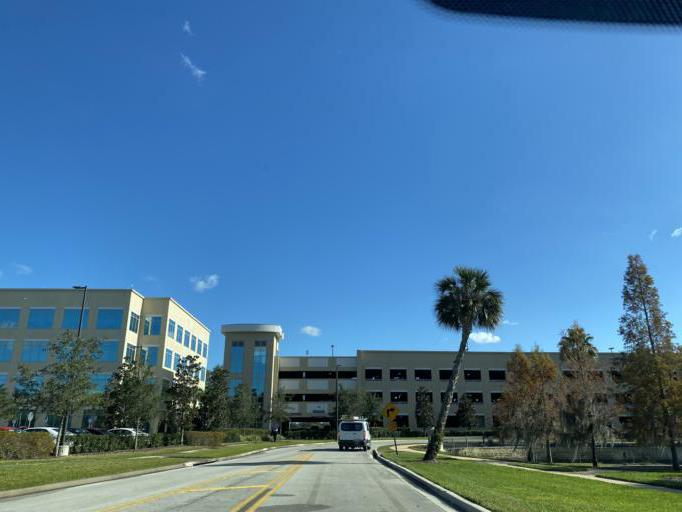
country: US
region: Florida
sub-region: Seminole County
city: Heathrow
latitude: 28.7926
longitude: -81.3525
